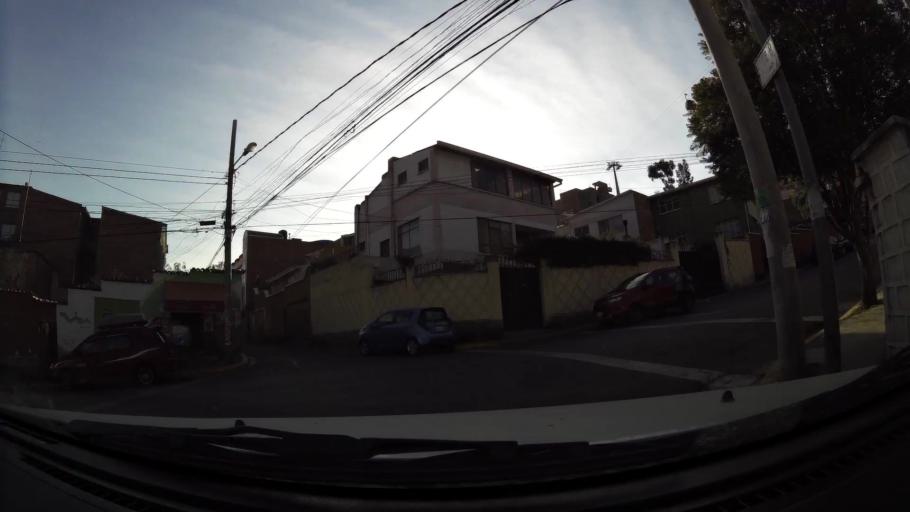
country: BO
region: La Paz
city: La Paz
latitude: -16.5261
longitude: -68.1030
